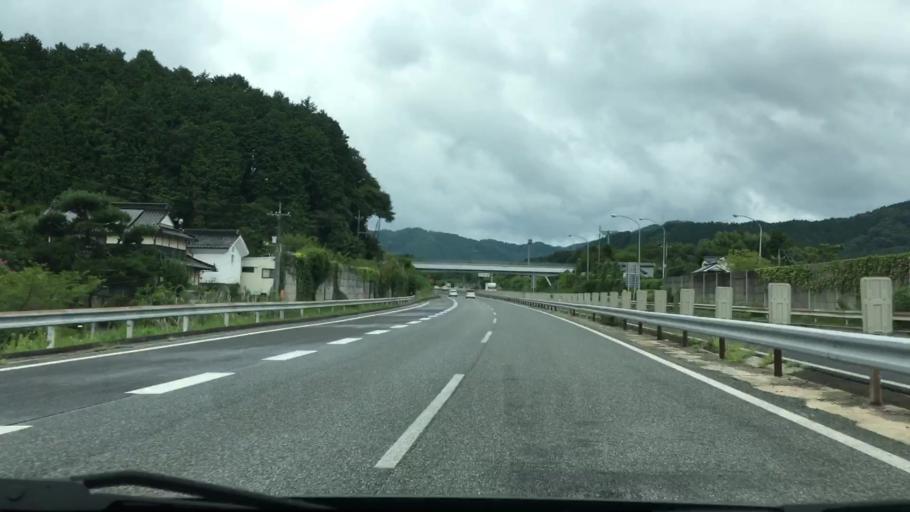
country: JP
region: Okayama
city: Tsuyama
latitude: 35.0252
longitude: 133.7467
